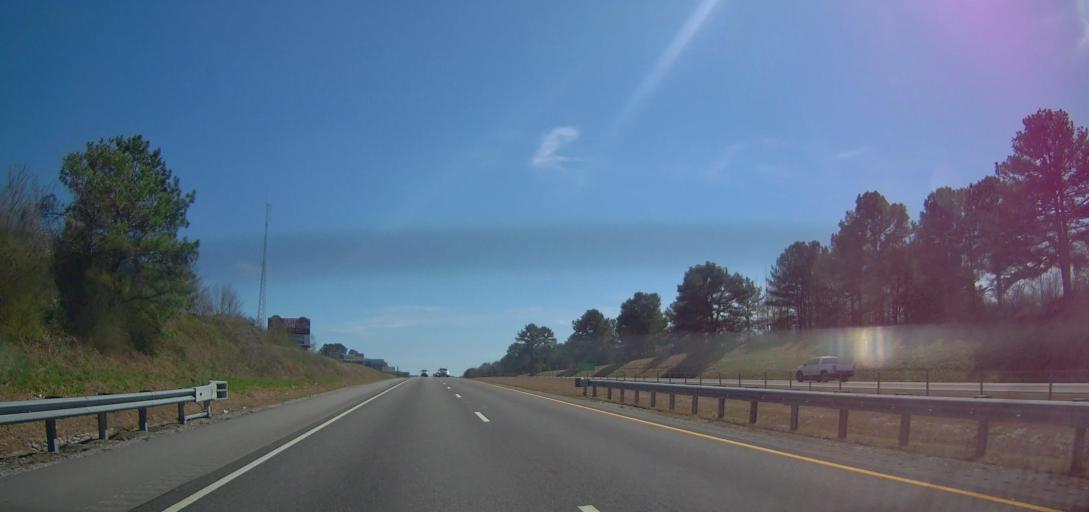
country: US
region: Alabama
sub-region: Cullman County
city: Cullman
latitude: 34.2496
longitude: -86.8882
